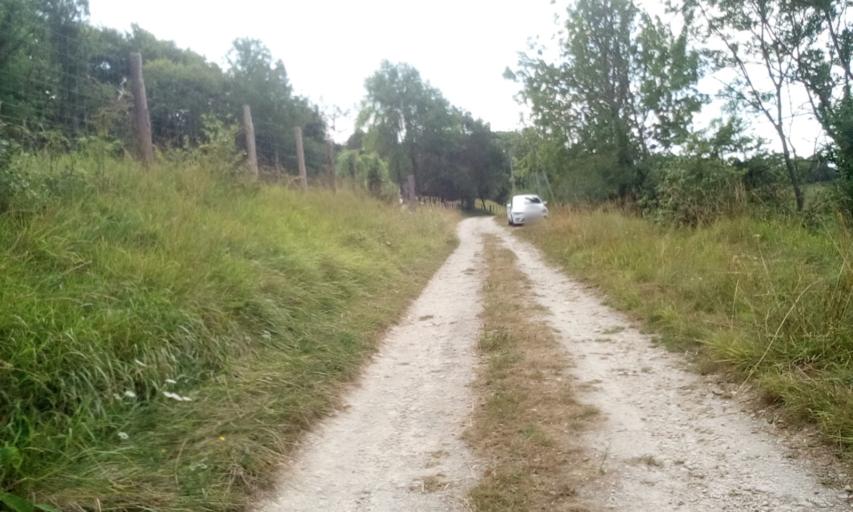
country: FR
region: Lower Normandy
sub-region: Departement du Calvados
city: Creully
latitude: 49.2855
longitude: -0.5223
